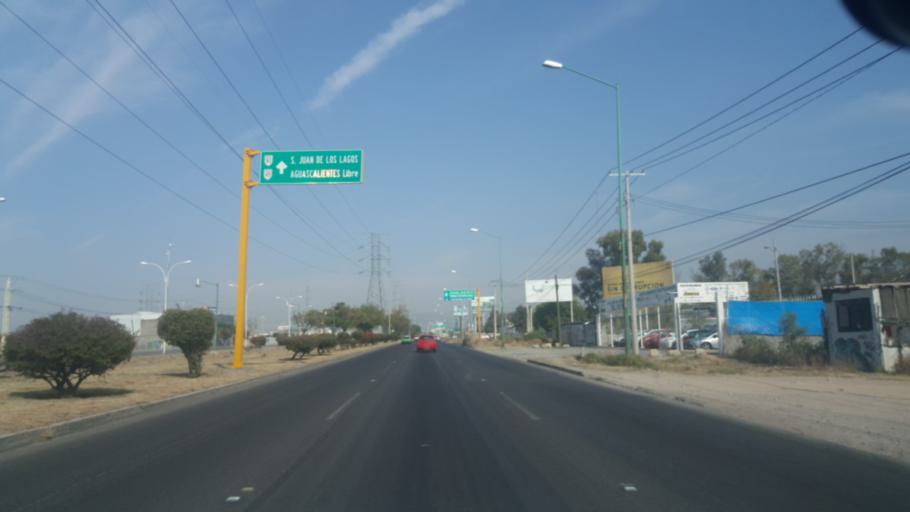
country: MX
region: Guanajuato
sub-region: Leon
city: Medina
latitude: 21.1330
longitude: -101.6304
